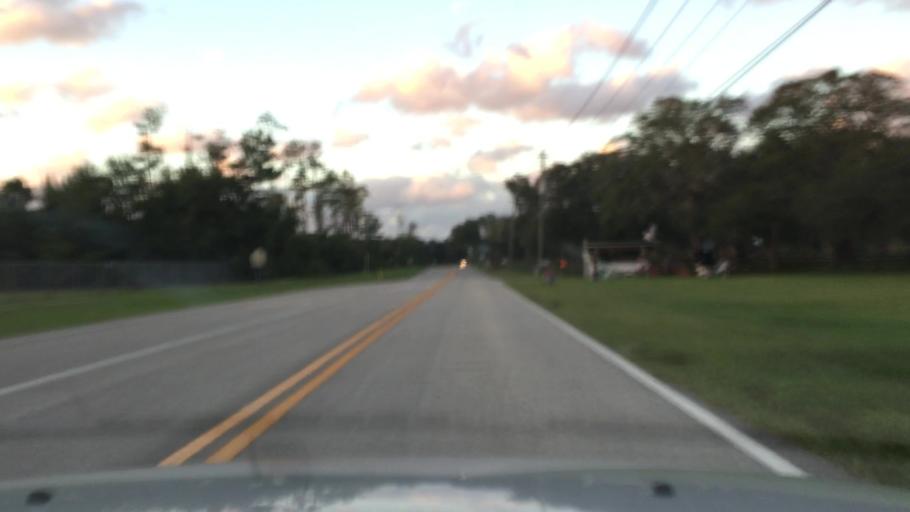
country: US
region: Florida
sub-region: Volusia County
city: Ormond Beach
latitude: 29.2773
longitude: -81.1129
